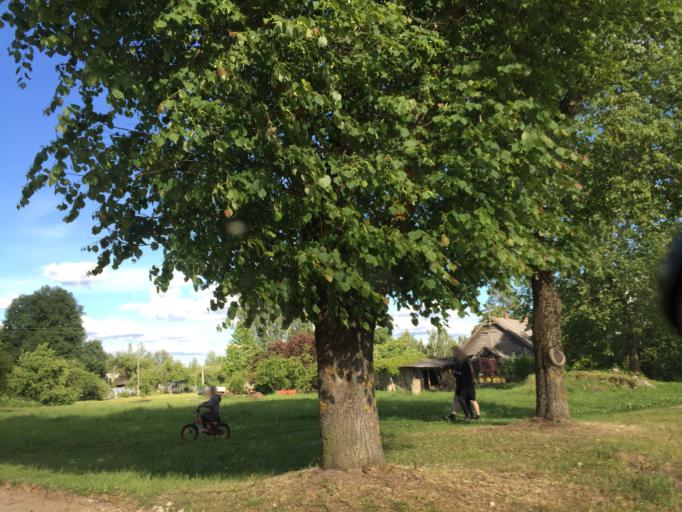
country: LV
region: Vecumnieki
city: Vecumnieki
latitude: 56.4507
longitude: 24.6003
